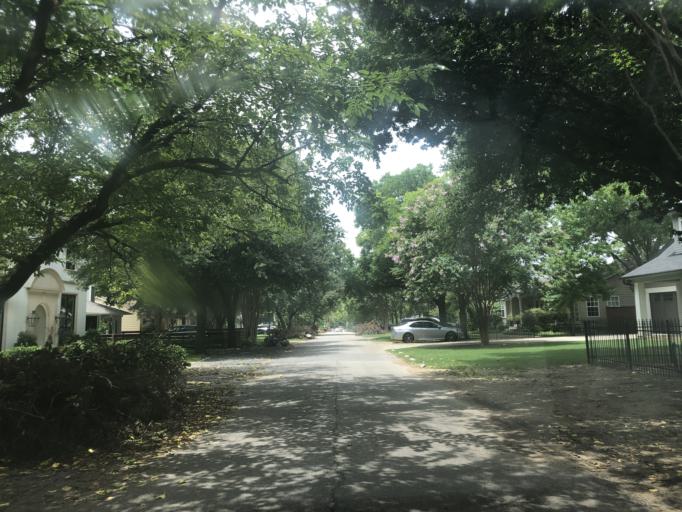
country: US
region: Texas
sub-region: Dallas County
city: University Park
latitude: 32.8562
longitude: -96.8232
